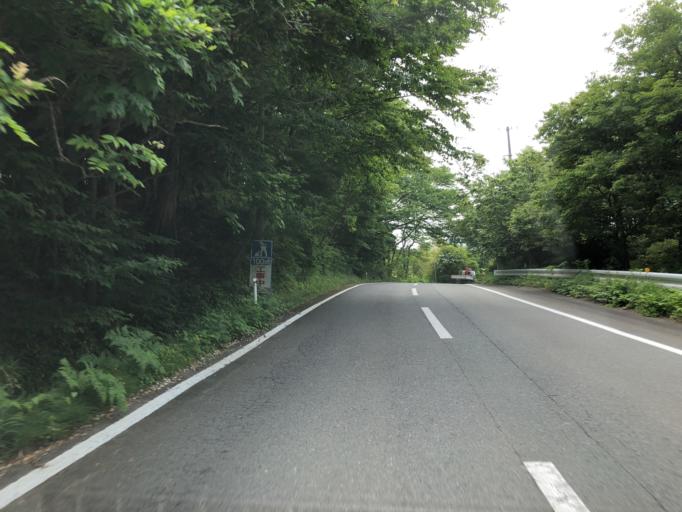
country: JP
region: Fukushima
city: Namie
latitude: 37.3023
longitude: 141.0044
